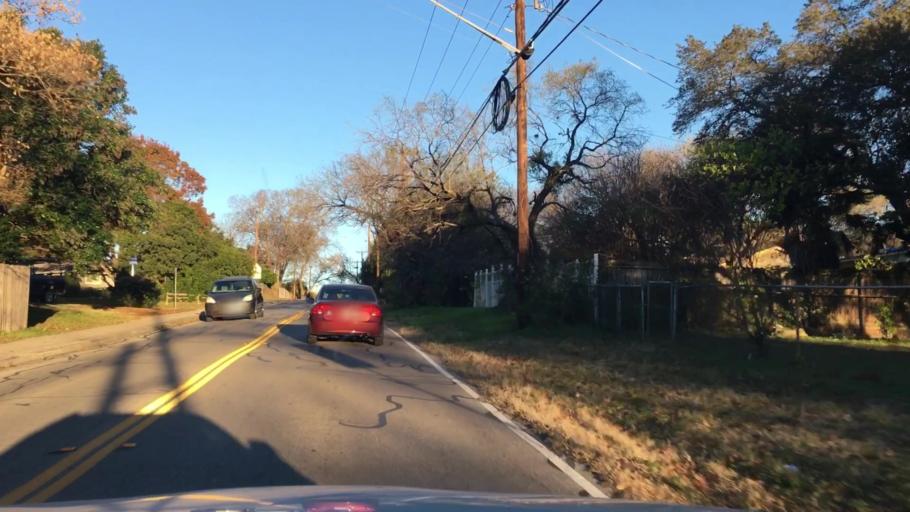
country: US
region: Texas
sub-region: Bexar County
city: Castle Hills
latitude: 29.5355
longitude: -98.5019
